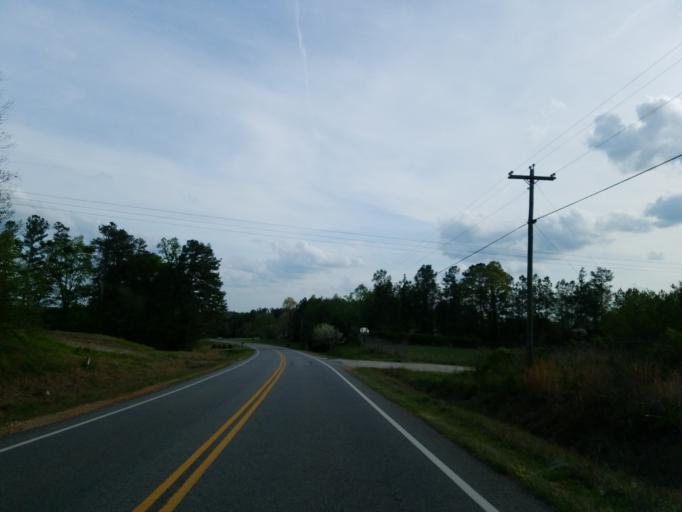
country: US
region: Georgia
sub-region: Cherokee County
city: Ball Ground
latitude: 34.3416
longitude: -84.2654
